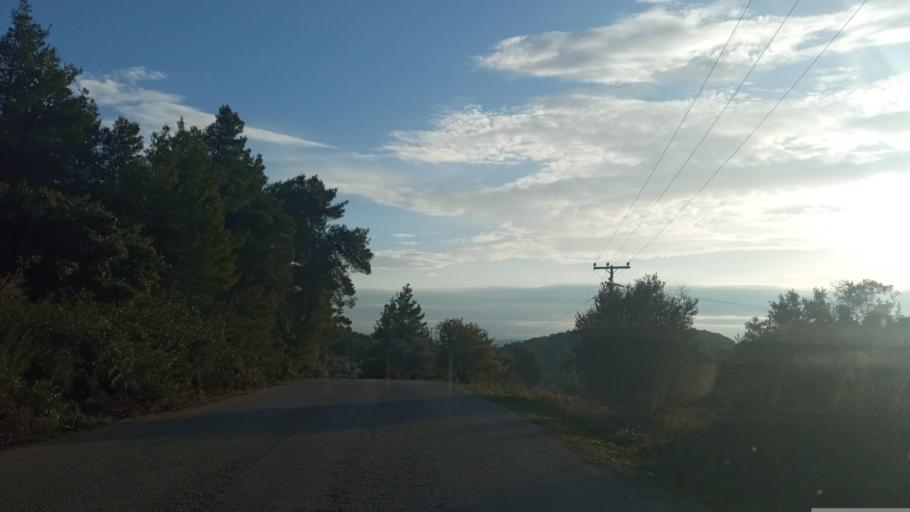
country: GR
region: Central Greece
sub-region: Nomos Evvoias
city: Psachna
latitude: 38.6107
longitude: 23.7299
